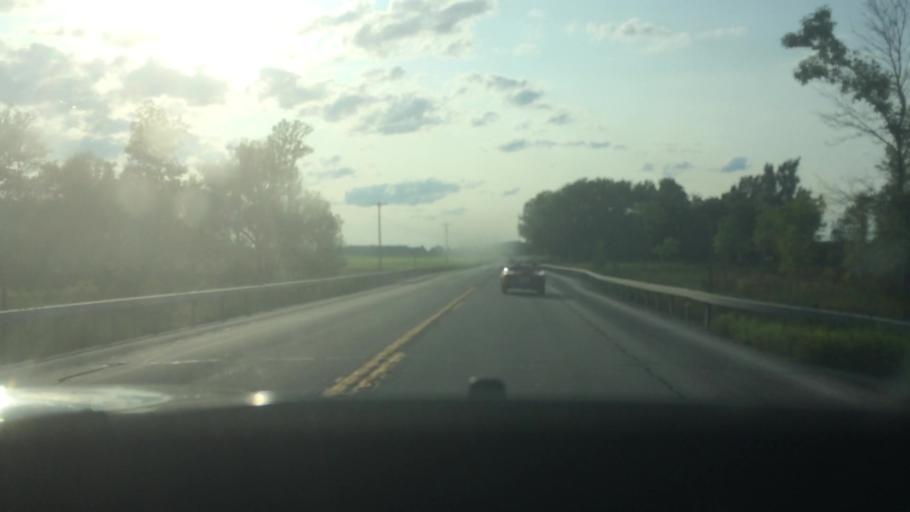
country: US
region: New York
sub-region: St. Lawrence County
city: Ogdensburg
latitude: 44.6606
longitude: -75.3344
